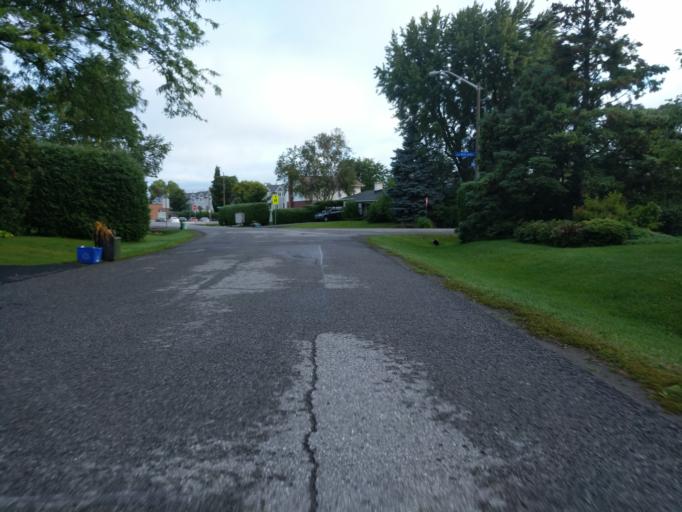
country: CA
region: Ontario
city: Bells Corners
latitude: 45.3466
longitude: -75.8224
